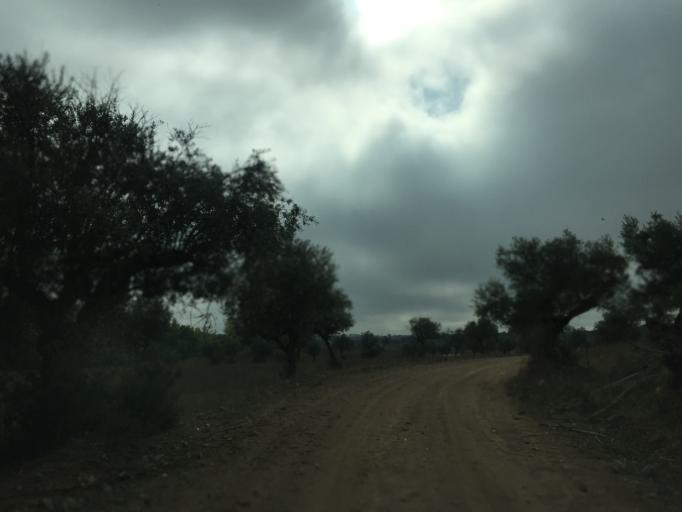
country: PT
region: Portalegre
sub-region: Fronteira
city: Fronteira
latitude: 39.0612
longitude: -7.6310
